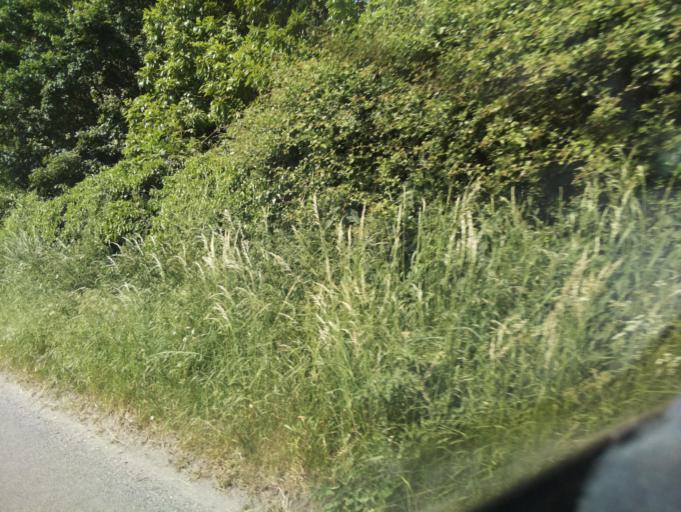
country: GB
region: England
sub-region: Hampshire
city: Abbotts Ann
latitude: 51.2421
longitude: -1.5694
